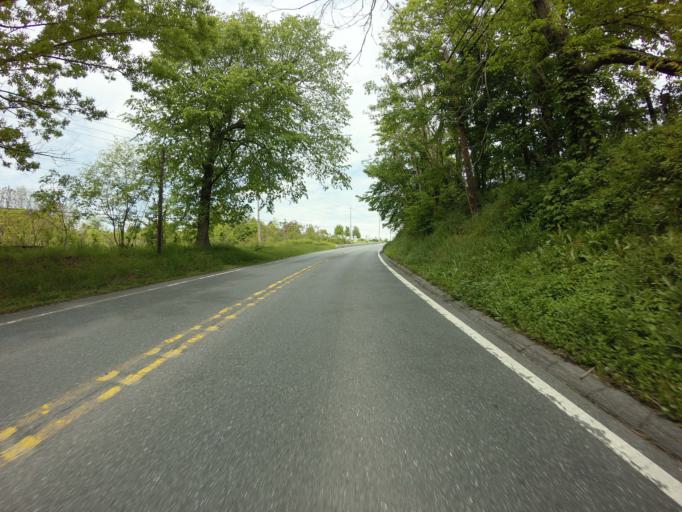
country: US
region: Maryland
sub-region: Frederick County
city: Urbana
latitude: 39.3189
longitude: -77.3348
